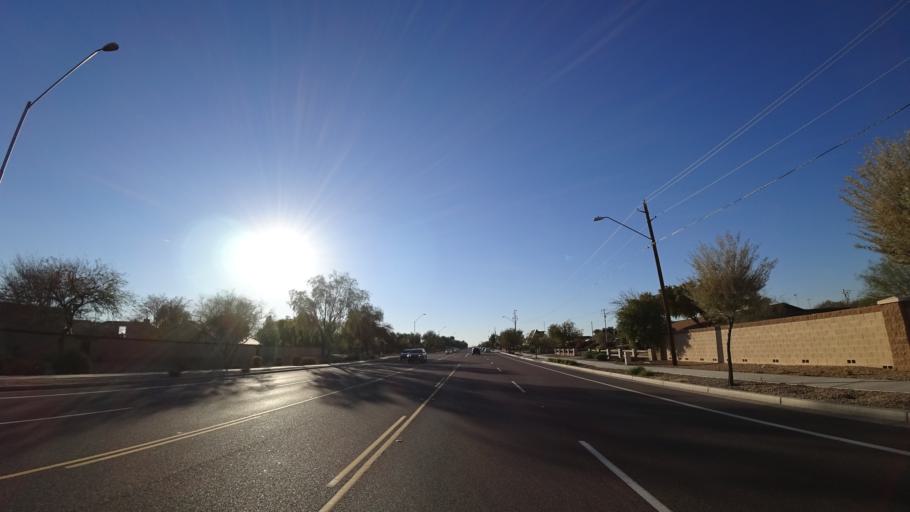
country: US
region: Arizona
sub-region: Maricopa County
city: Sun City
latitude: 33.6817
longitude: -112.2449
